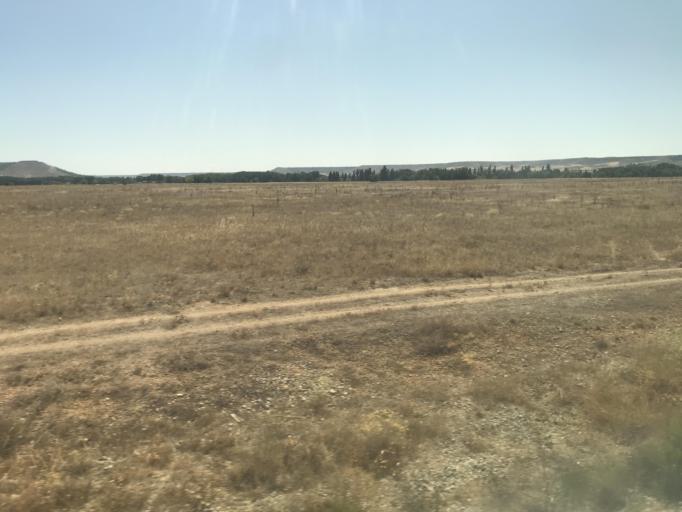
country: ES
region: Castille and Leon
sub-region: Provincia de Valladolid
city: Cubillas de Santa Marta
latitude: 41.8237
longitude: -4.5703
